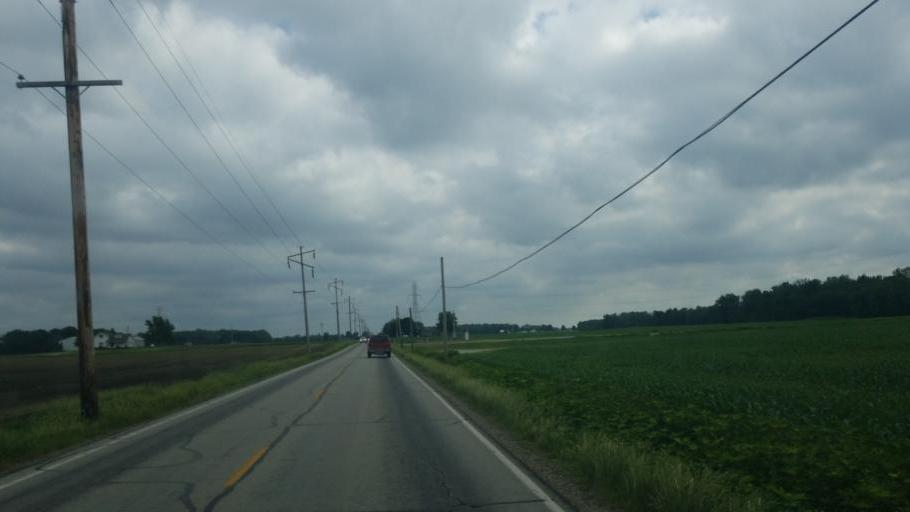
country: US
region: Indiana
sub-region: Elkhart County
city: Nappanee
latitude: 41.4063
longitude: -86.0011
